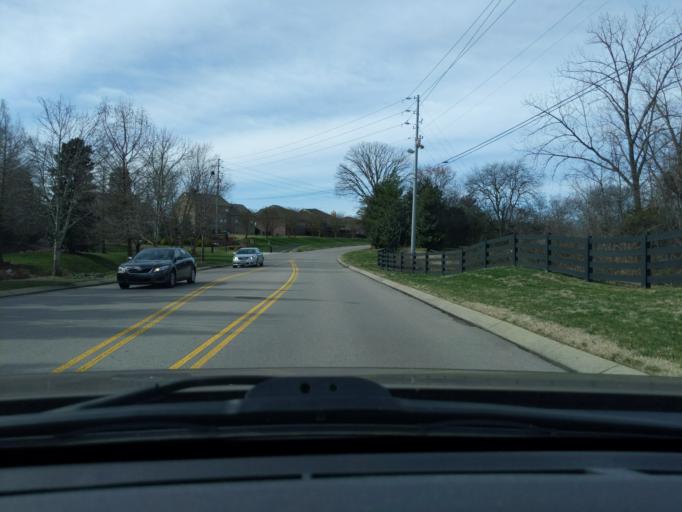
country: US
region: Tennessee
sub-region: Wilson County
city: Mount Juliet
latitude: 36.1672
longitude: -86.4858
